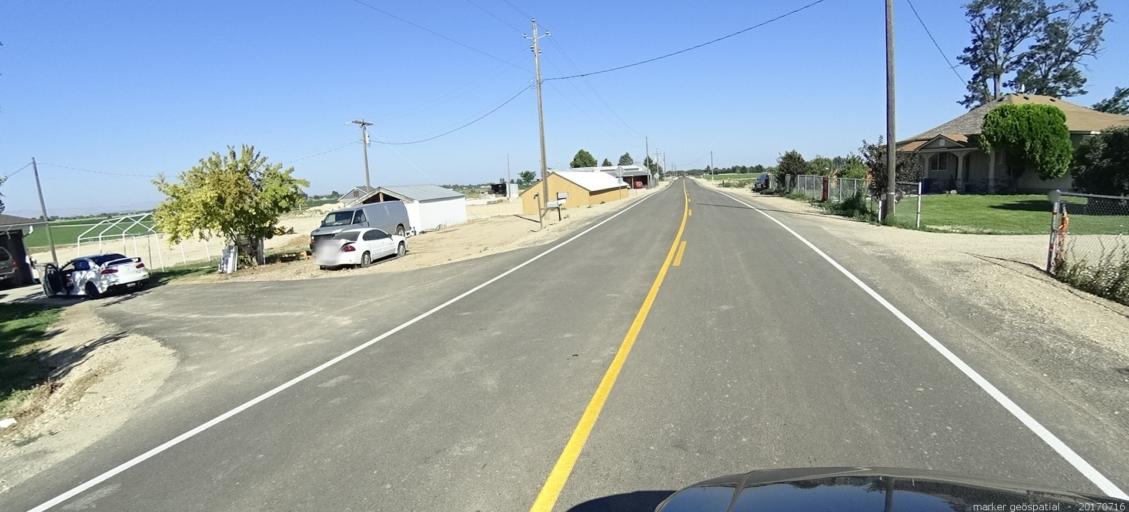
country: US
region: Idaho
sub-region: Canyon County
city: Nampa
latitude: 43.5470
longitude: -116.4846
